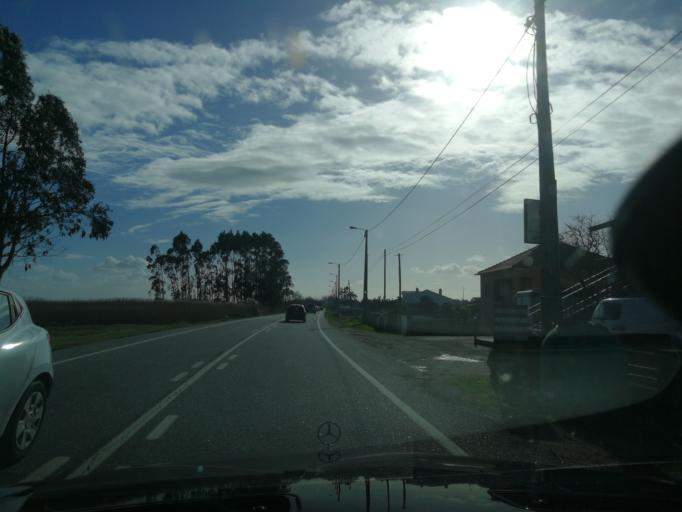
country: PT
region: Aveiro
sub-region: Estarreja
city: Pardilho
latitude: 40.8053
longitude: -8.6726
